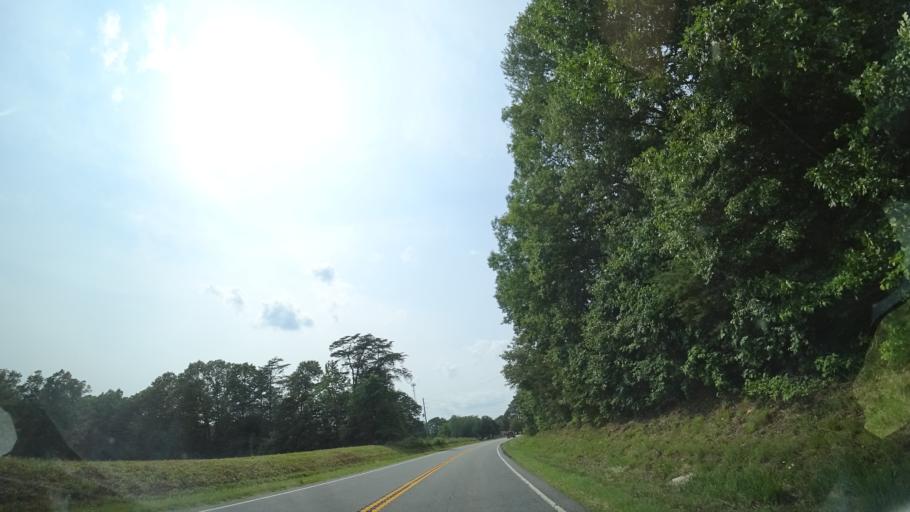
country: US
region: Virginia
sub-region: Spotsylvania County
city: Spotsylvania Courthouse
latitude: 38.1155
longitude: -77.7555
